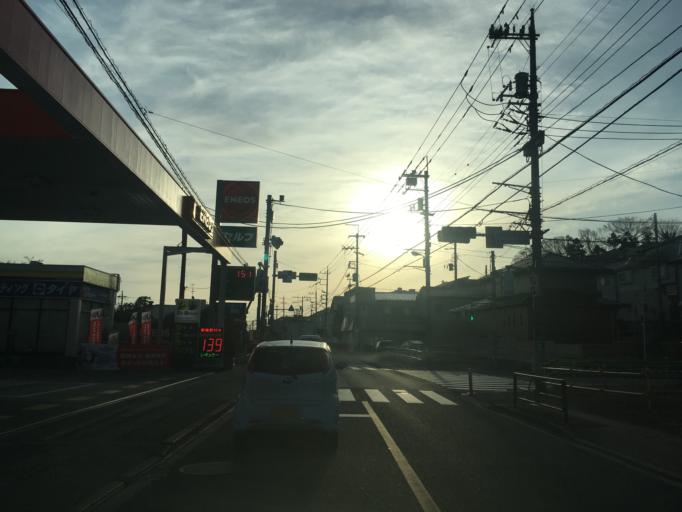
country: JP
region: Tokyo
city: Hino
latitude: 35.6591
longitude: 139.4164
